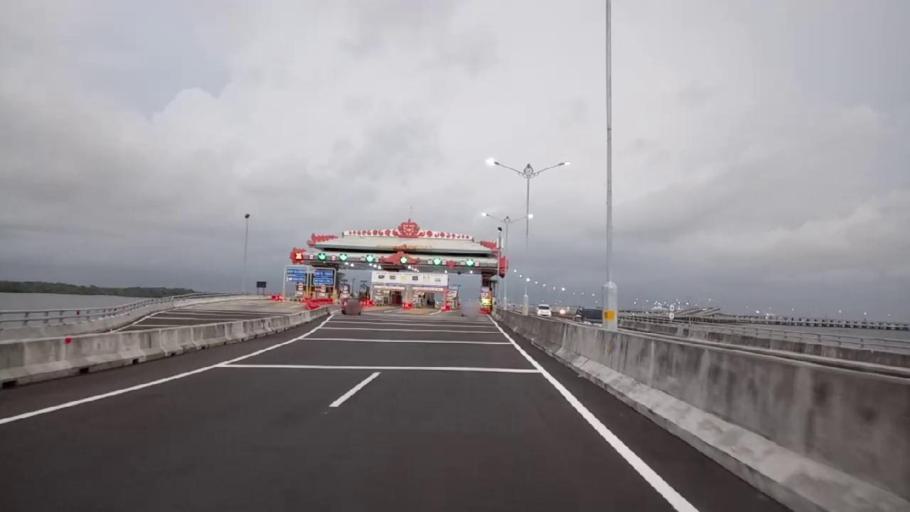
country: ID
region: Bali
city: Kelanabian
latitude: -8.7447
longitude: 115.1872
